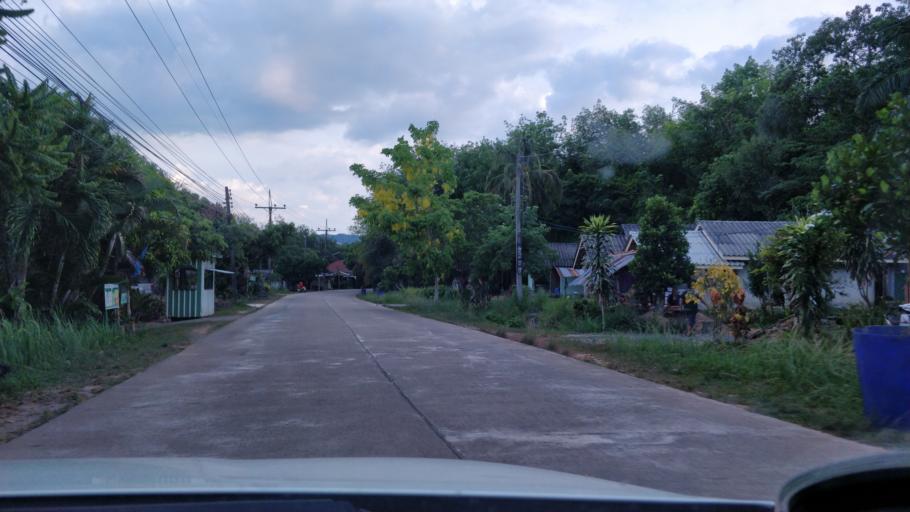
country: TH
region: Krabi
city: Saladan
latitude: 7.5879
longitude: 99.0689
